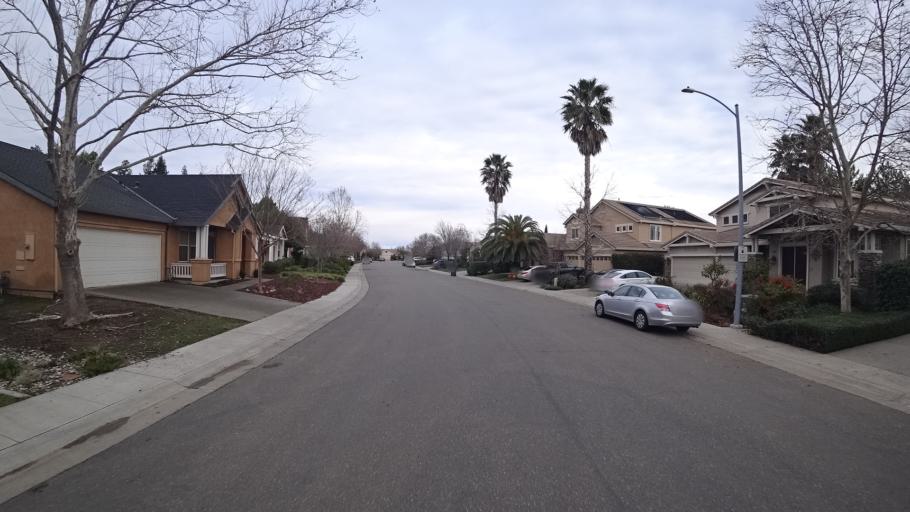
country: US
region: California
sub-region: Yolo County
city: Davis
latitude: 38.5695
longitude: -121.7242
